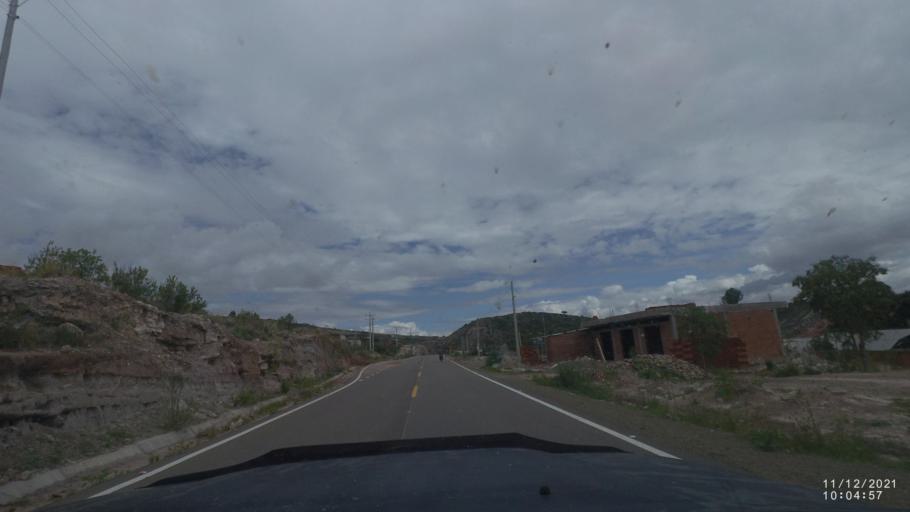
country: BO
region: Cochabamba
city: Cliza
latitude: -17.7046
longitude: -65.9457
